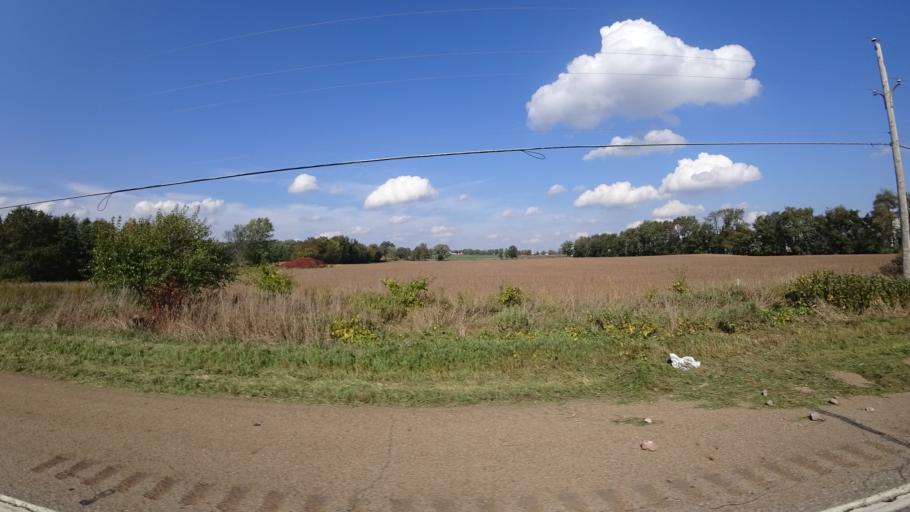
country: US
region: Michigan
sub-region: Jackson County
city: Concord
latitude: 42.1628
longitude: -84.7176
